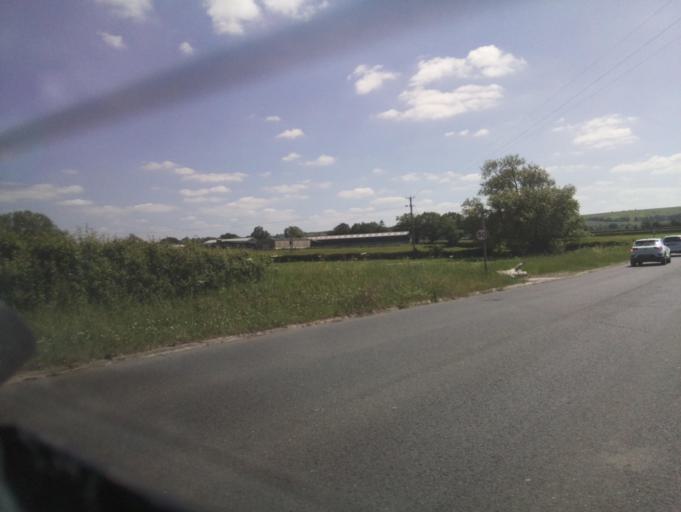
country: GB
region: England
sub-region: Borough of Swindon
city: Wroughton
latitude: 51.5383
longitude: -1.8098
